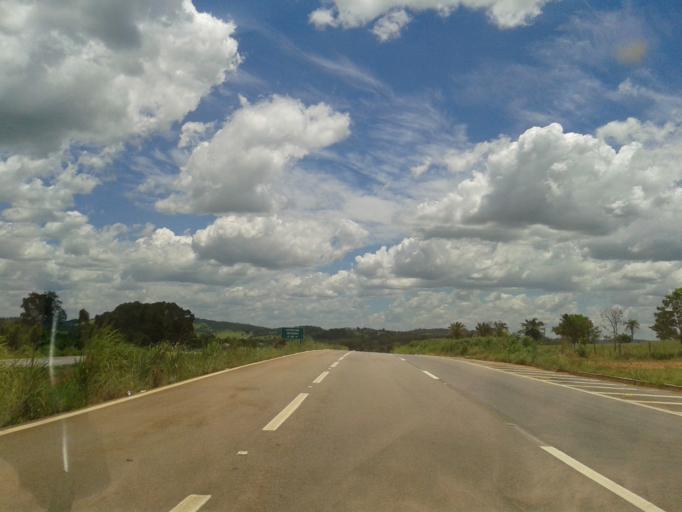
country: BR
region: Goias
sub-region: Neropolis
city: Neropolis
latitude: -16.2647
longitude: -49.3025
